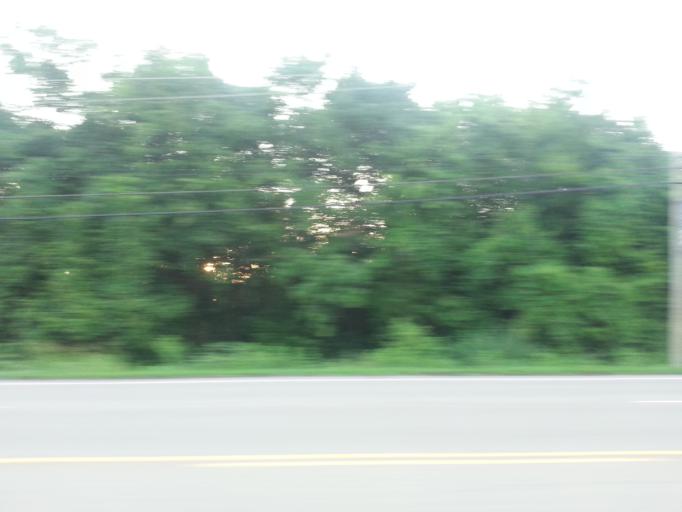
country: US
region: Tennessee
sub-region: Knox County
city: Farragut
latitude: 35.8891
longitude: -84.1481
